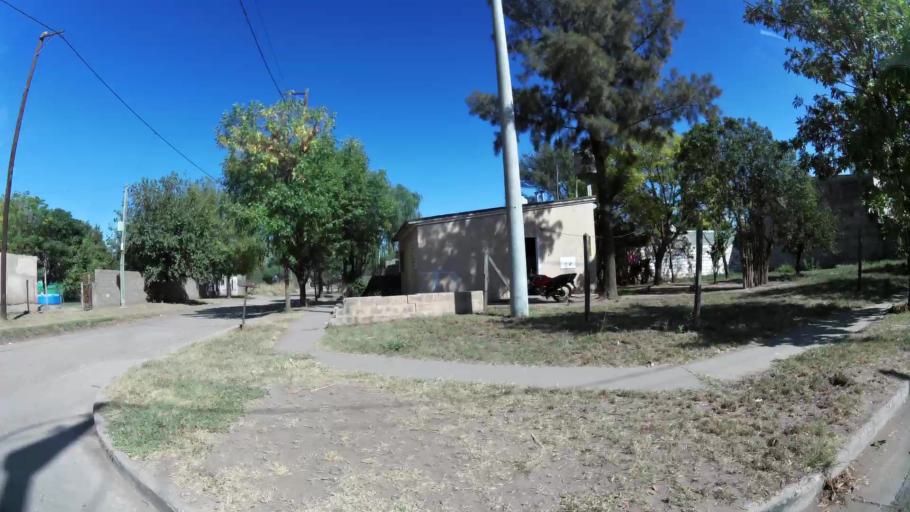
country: AR
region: Cordoba
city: Villa Allende
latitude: -31.3205
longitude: -64.2513
